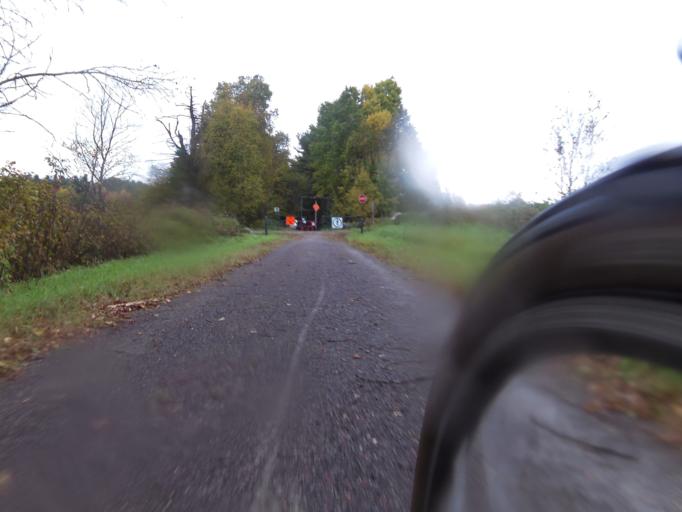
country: CA
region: Quebec
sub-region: Outaouais
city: Shawville
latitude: 45.6785
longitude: -76.5422
